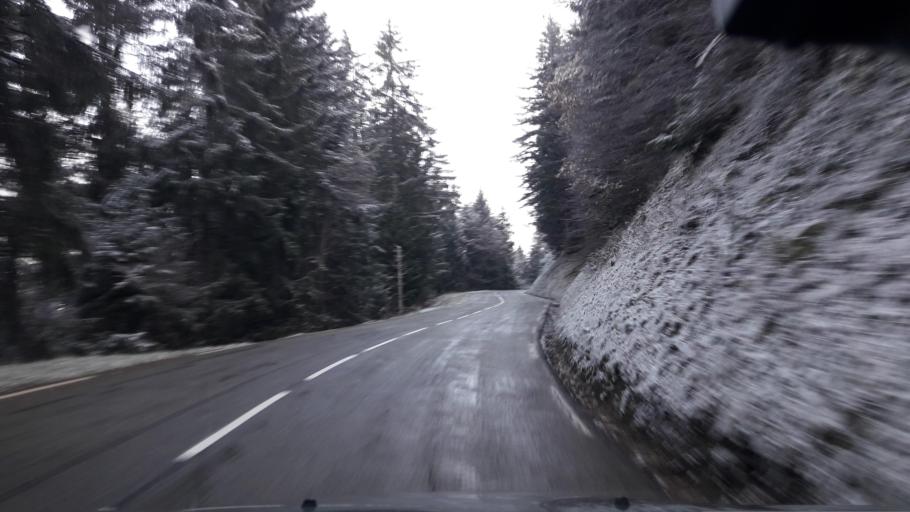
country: FR
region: Rhone-Alpes
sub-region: Departement de l'Isere
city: Allevard
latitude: 45.3941
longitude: 6.0899
